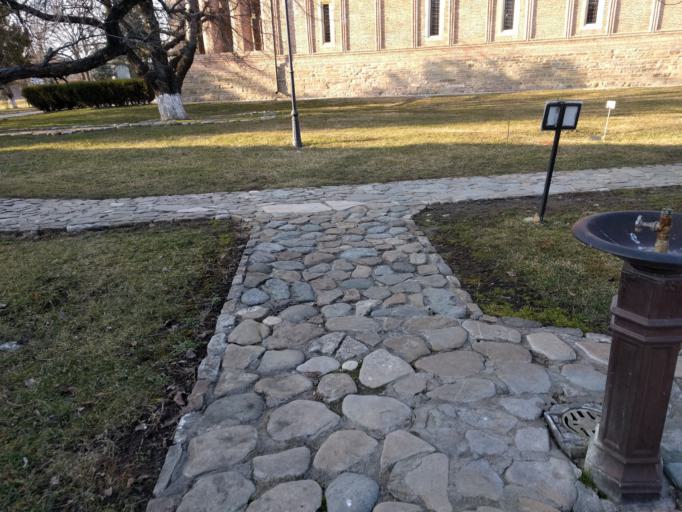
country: RO
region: Dambovita
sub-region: Municipiul Targoviste
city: Targoviste
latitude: 44.9315
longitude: 25.4591
